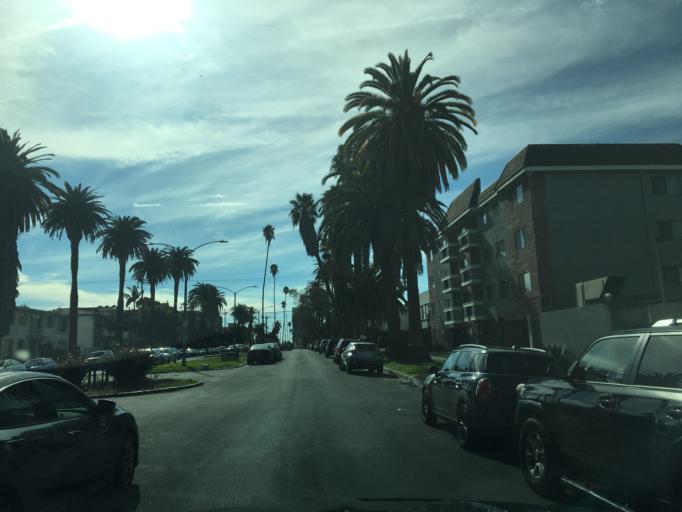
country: US
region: California
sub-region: Los Angeles County
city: Silver Lake
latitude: 34.0706
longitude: -118.2804
